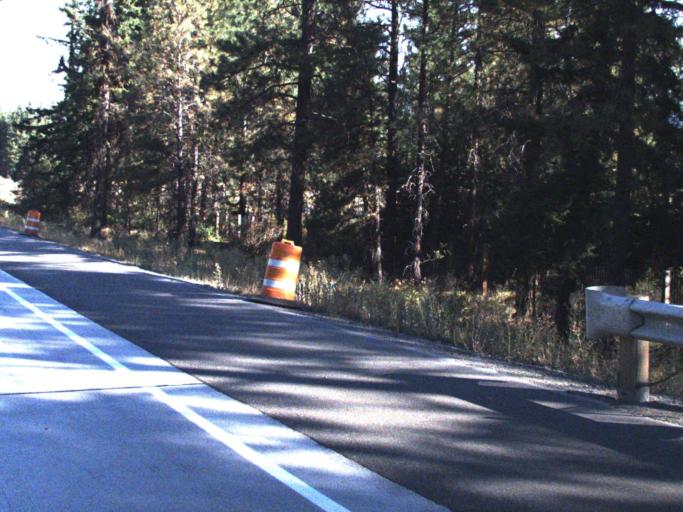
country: US
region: Washington
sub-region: Kittitas County
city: Cle Elum
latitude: 47.1529
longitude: -120.8208
